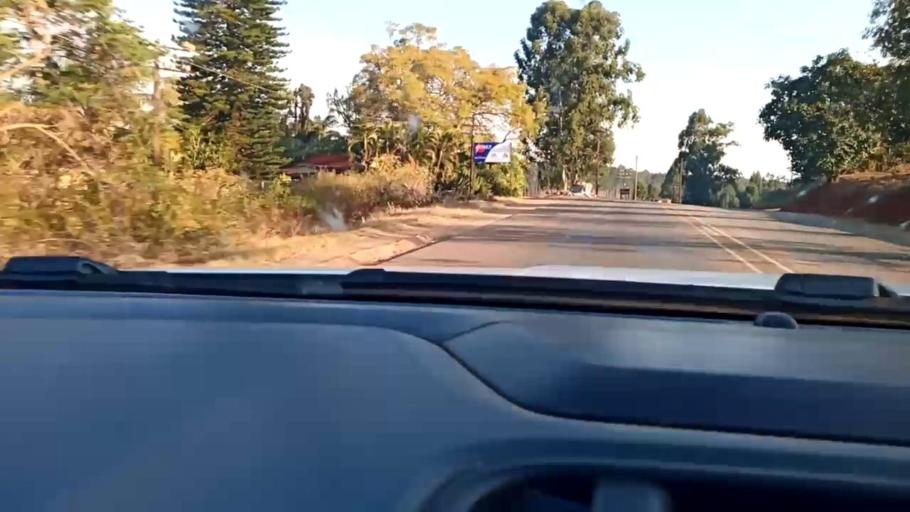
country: ZA
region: Limpopo
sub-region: Mopani District Municipality
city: Duiwelskloof
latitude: -23.6998
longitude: 30.1359
